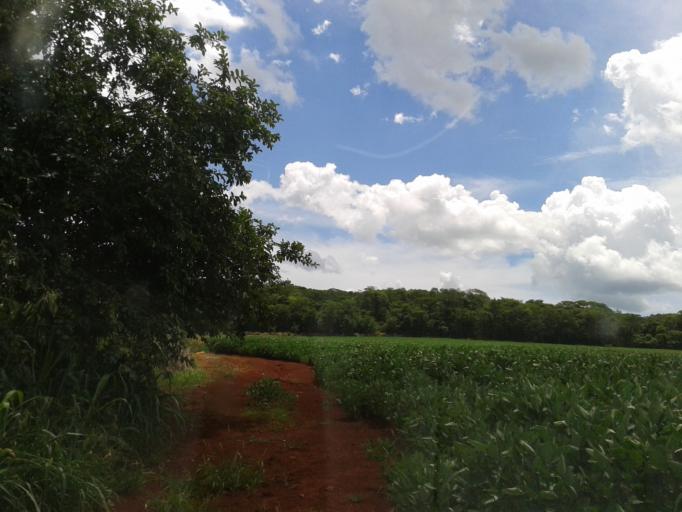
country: BR
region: Minas Gerais
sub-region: Centralina
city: Centralina
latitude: -18.6837
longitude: -49.2169
